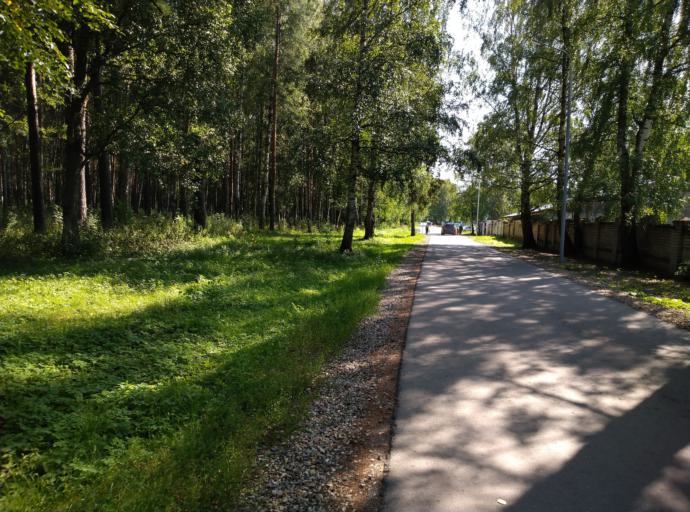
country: RU
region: Kostroma
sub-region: Kostromskoy Rayon
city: Kostroma
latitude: 57.7915
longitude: 40.9655
